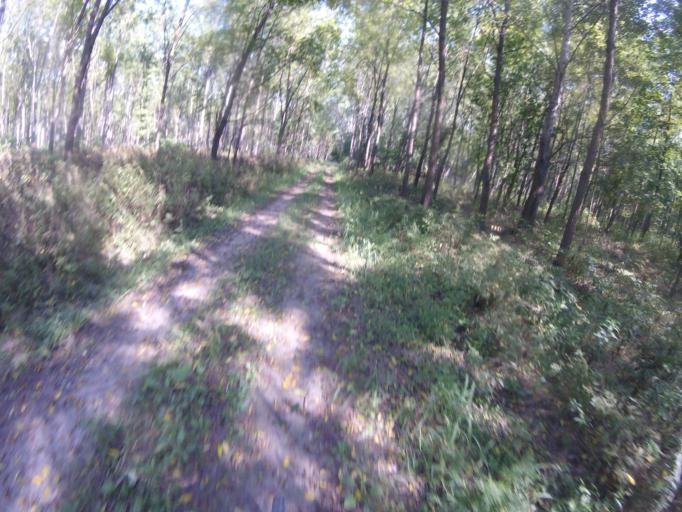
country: HU
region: Bacs-Kiskun
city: Baja
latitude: 46.2011
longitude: 18.8616
